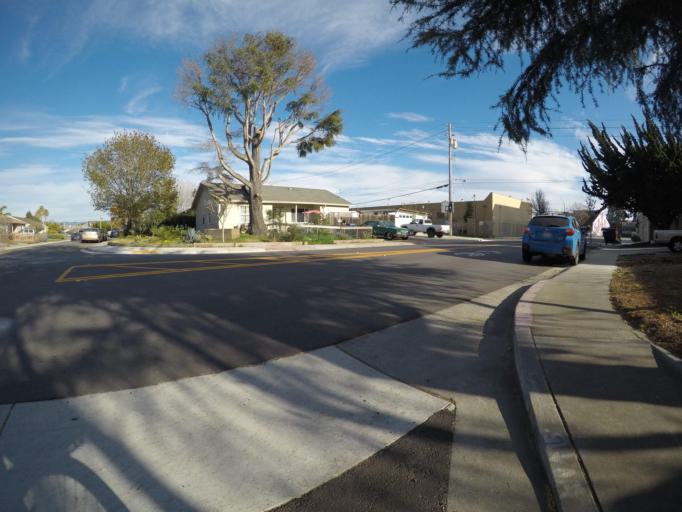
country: US
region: California
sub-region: Santa Cruz County
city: Santa Cruz
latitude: 36.9616
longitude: -122.0488
